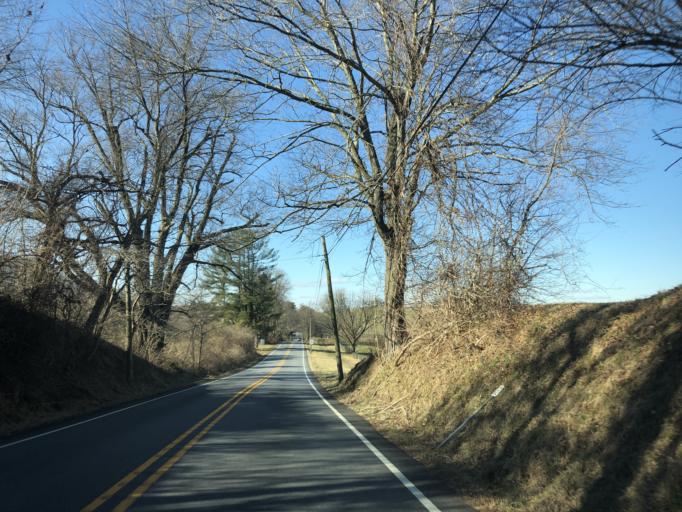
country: US
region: Pennsylvania
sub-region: Chester County
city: Upland
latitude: 39.9009
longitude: -75.7728
